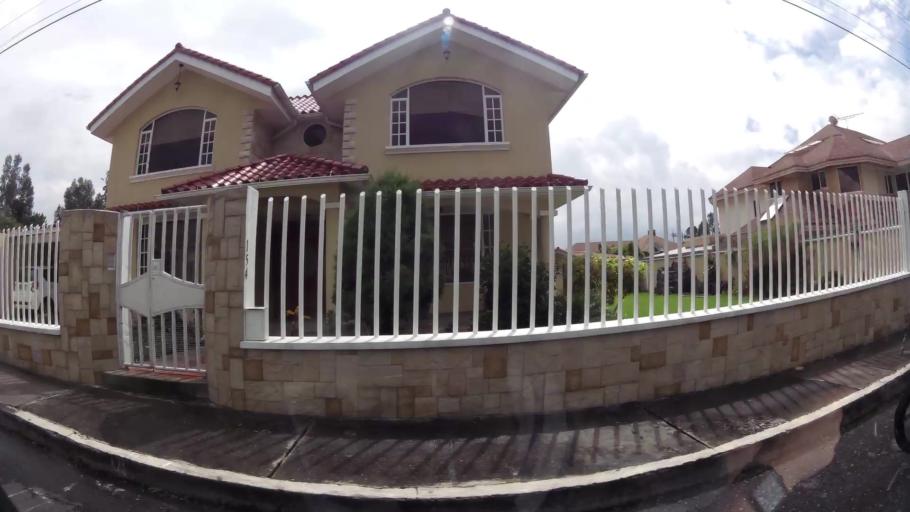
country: EC
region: Pichincha
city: Sangolqui
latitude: -0.3072
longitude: -78.4739
